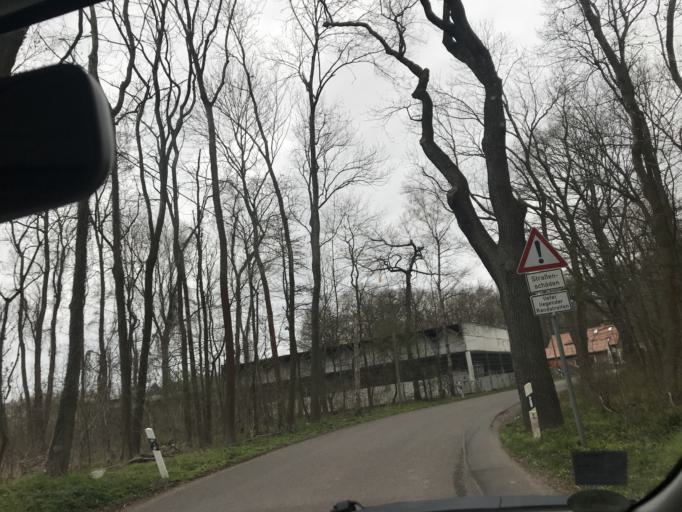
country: DE
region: Saxony
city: Schkeuditz
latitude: 51.3660
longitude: 12.2566
